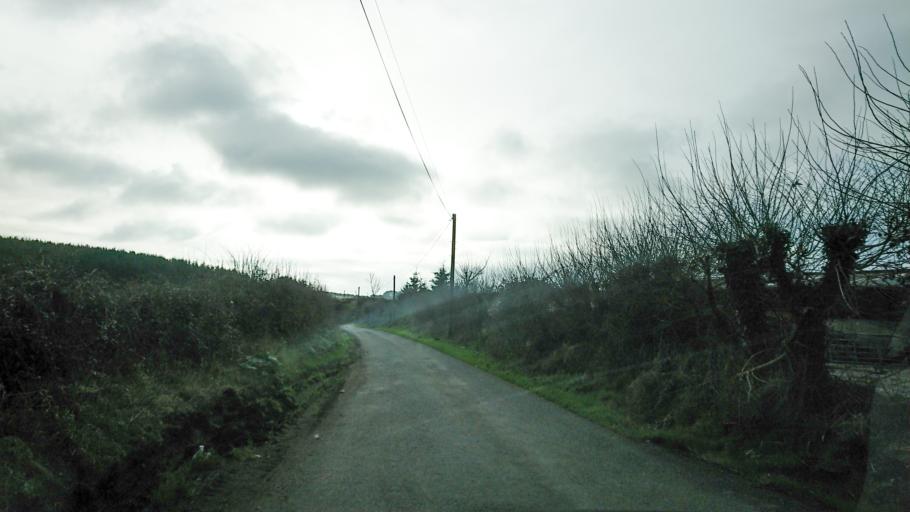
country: IE
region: Munster
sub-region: Waterford
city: Tra Mhor
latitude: 52.1882
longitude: -7.1753
